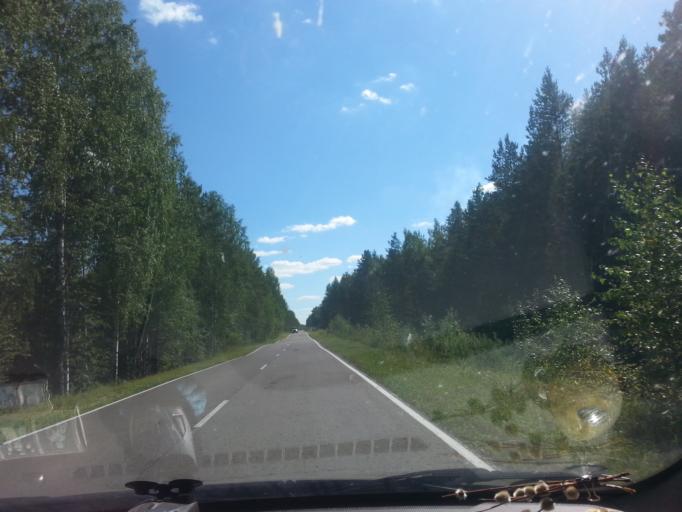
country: RU
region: Vladimir
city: Galitsy
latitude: 56.0747
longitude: 42.8673
